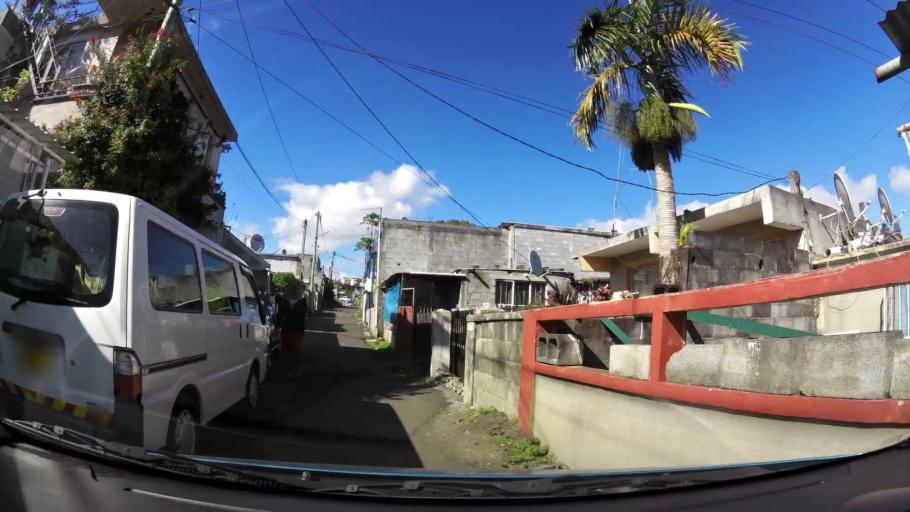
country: MU
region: Plaines Wilhems
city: Curepipe
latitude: -20.3034
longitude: 57.5039
